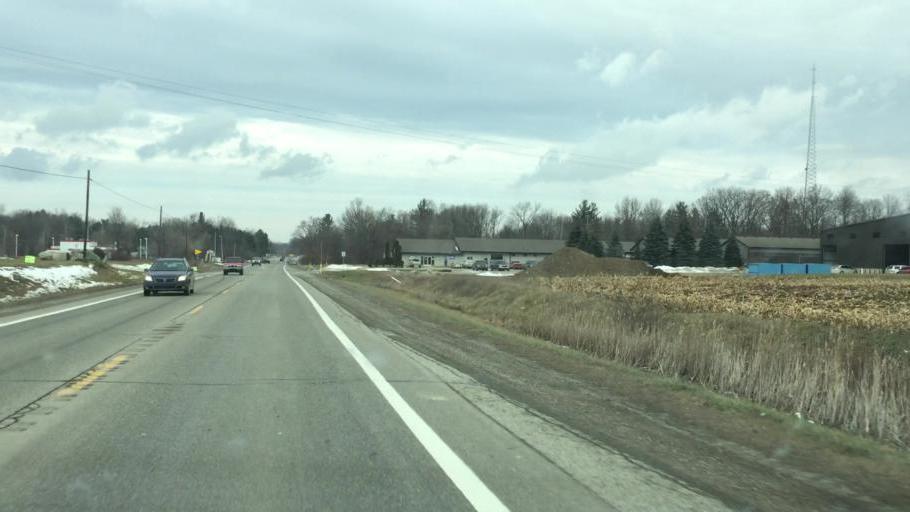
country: US
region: Michigan
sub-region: Lapeer County
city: Barnes Lake-Millers Lake
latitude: 43.1949
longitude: -83.3127
